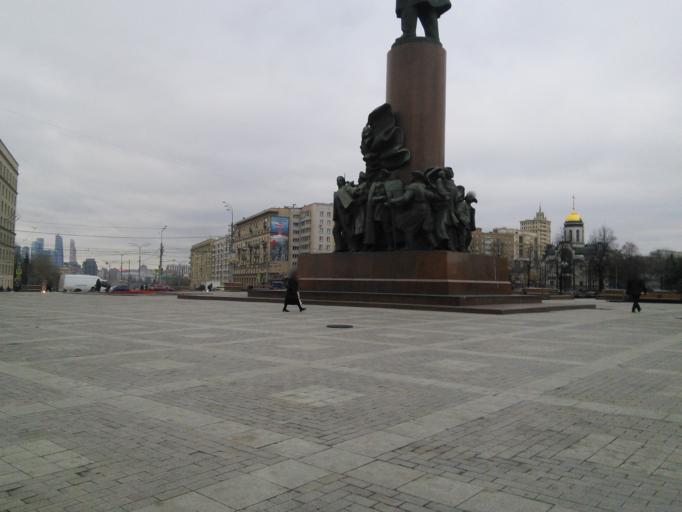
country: RU
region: Moscow
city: Zamoskvorech'ye
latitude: 55.7292
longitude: 37.6135
